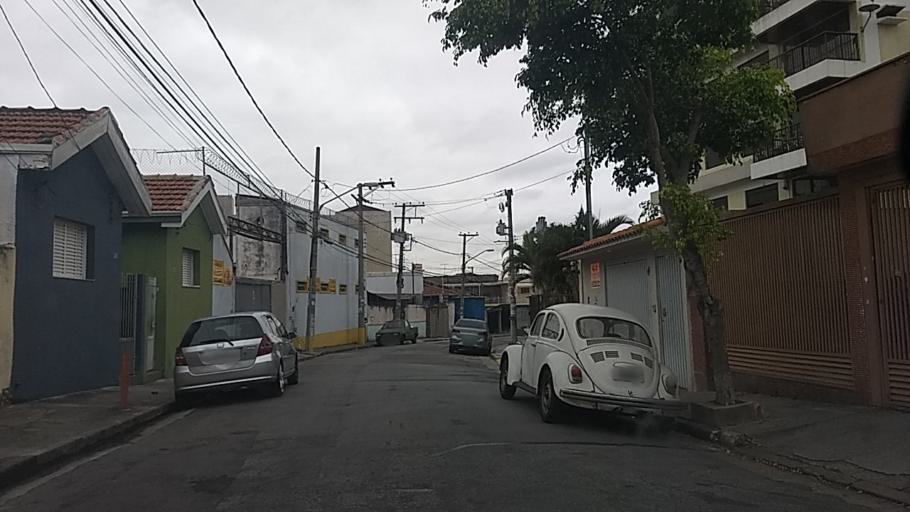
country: BR
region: Sao Paulo
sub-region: Sao Paulo
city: Sao Paulo
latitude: -23.5106
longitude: -46.5890
